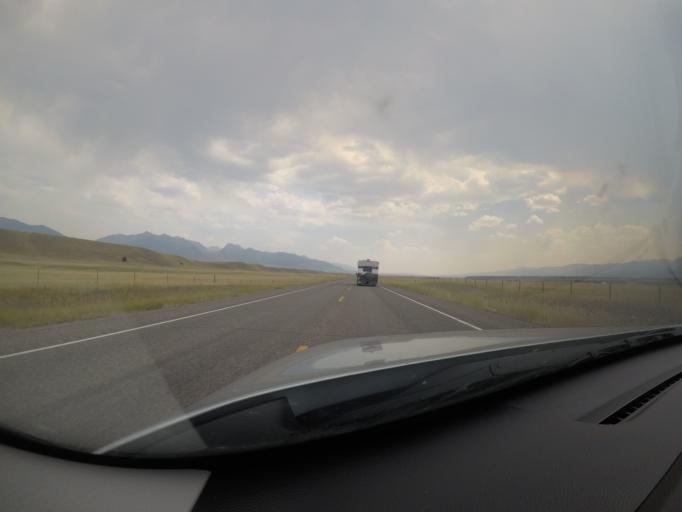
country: US
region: Montana
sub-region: Madison County
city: Virginia City
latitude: 45.1293
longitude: -111.6677
